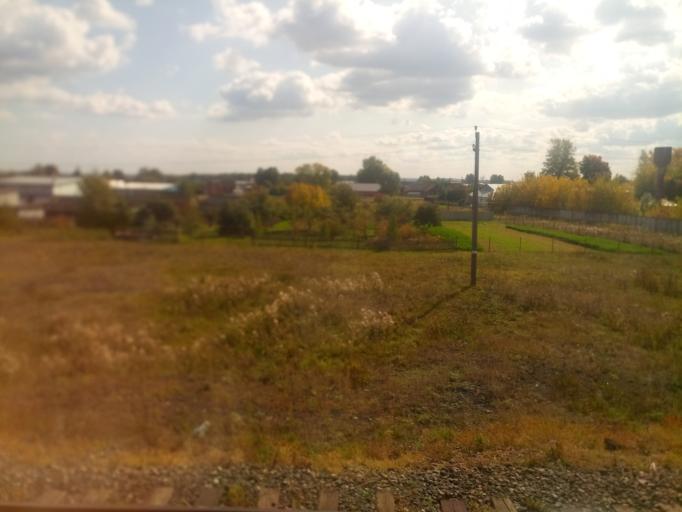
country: RU
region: Chuvashia
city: Urmary
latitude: 55.6888
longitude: 47.9511
